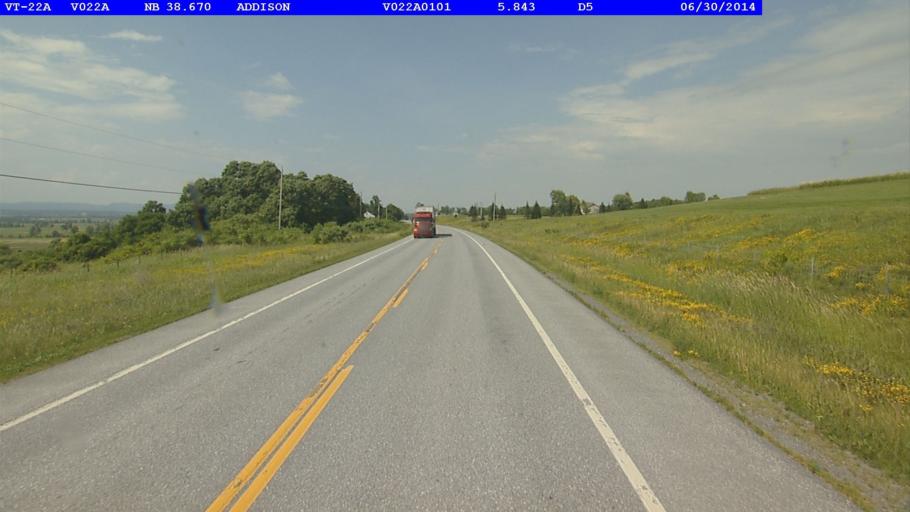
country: US
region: Vermont
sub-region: Addison County
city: Vergennes
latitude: 44.1128
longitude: -73.2938
